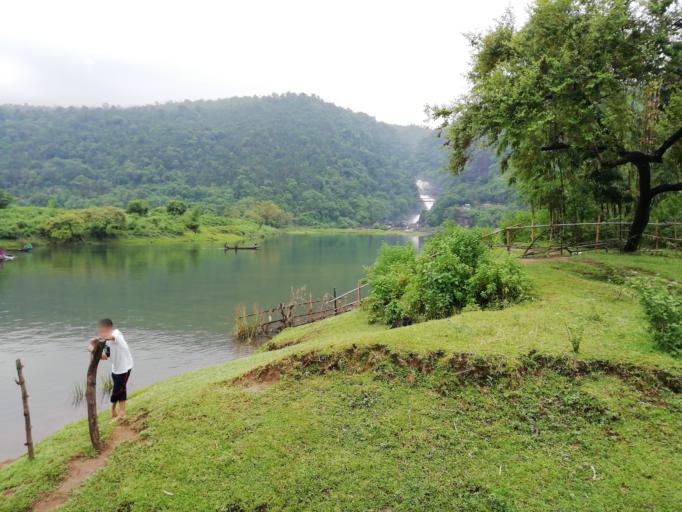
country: IN
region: Meghalaya
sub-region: East Khasi Hills
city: Cherrapunji
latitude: 25.1776
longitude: 91.9557
